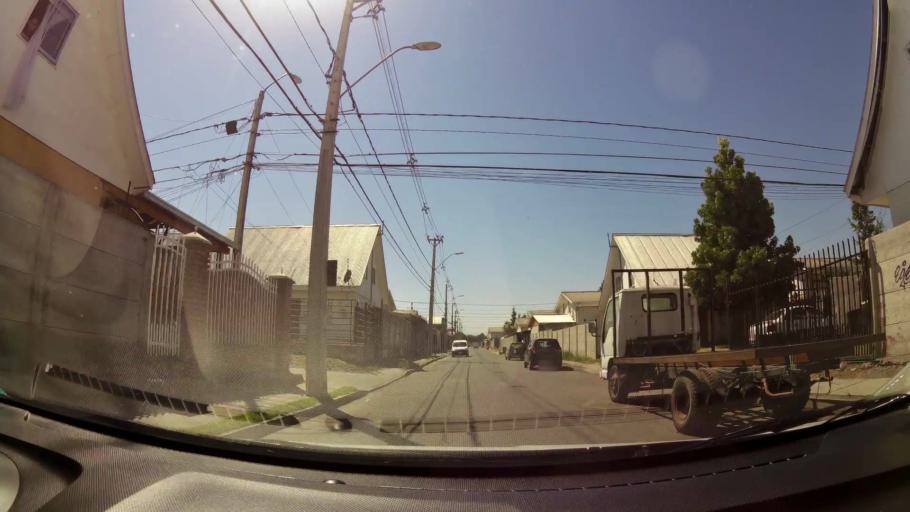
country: CL
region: Maule
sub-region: Provincia de Curico
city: Curico
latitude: -34.9654
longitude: -71.2471
